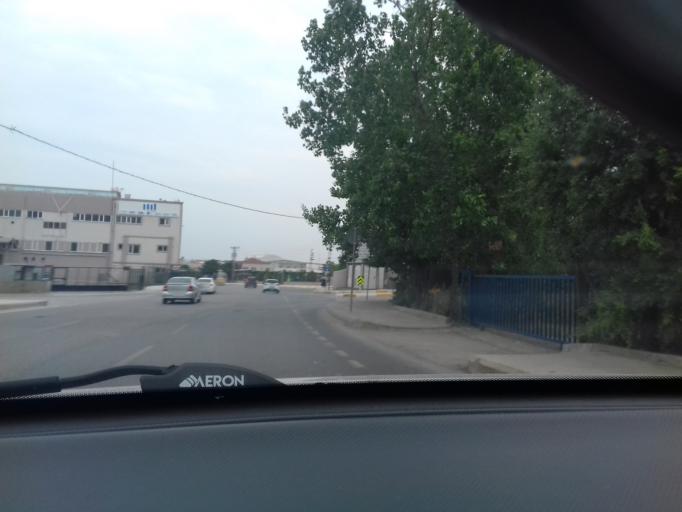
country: TR
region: Istanbul
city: Pendik
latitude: 40.9089
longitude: 29.2965
